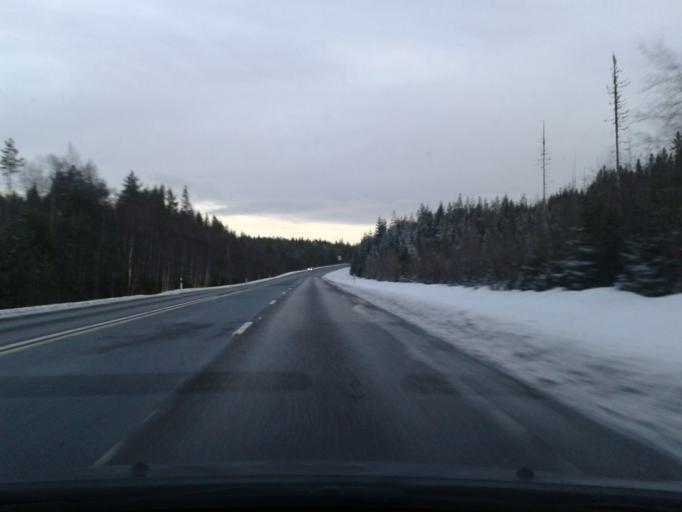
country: SE
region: Vaesternorrland
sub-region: Solleftea Kommun
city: Solleftea
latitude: 63.1273
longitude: 17.4803
